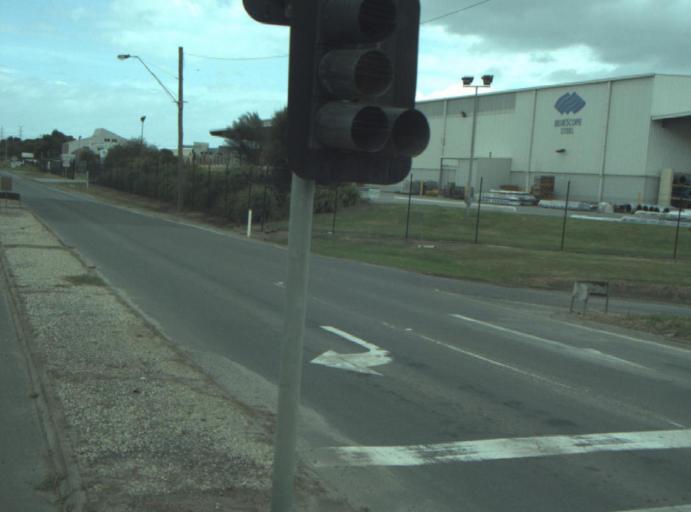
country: AU
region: Victoria
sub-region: Greater Geelong
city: Leopold
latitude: -38.1670
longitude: 144.4224
